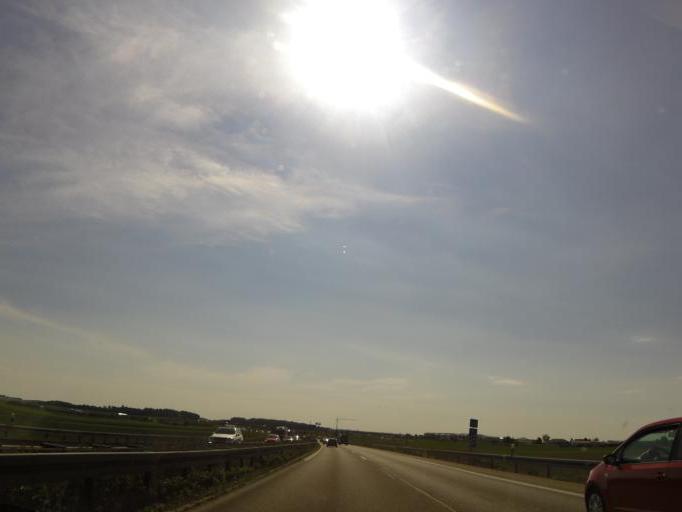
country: DE
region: Baden-Wuerttemberg
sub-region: Tuebingen Region
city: Merklingen
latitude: 48.5194
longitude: 9.7486
